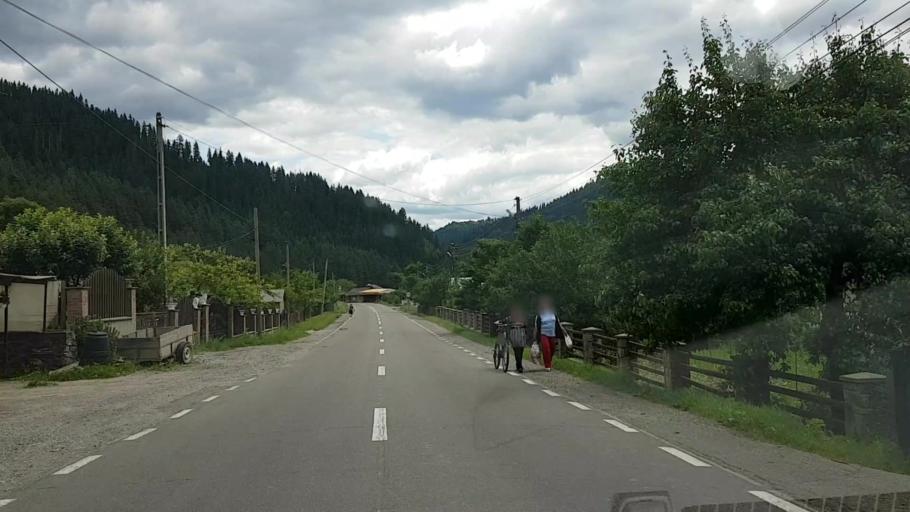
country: RO
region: Neamt
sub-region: Comuna Poiana Teiului
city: Poiana Teiului
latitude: 47.1295
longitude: 25.9018
